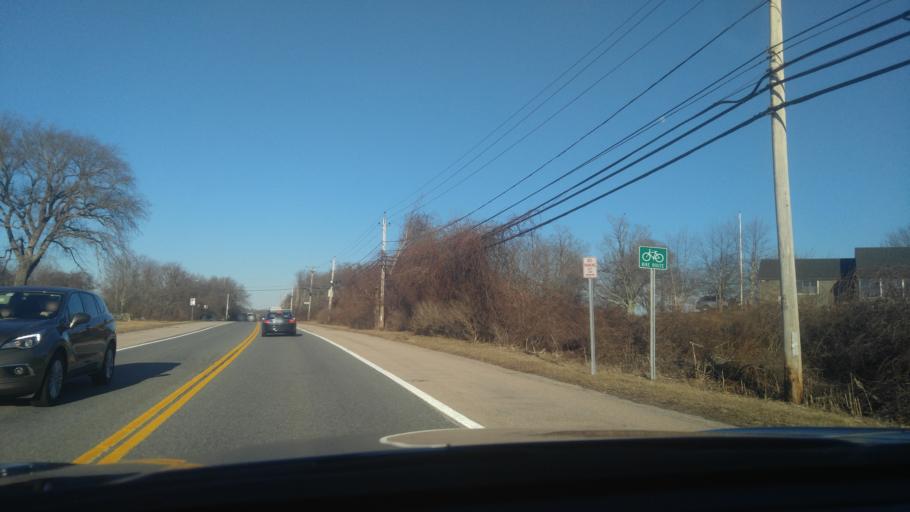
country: US
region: Rhode Island
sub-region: Washington County
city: Narragansett Pier
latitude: 41.4522
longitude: -71.4442
